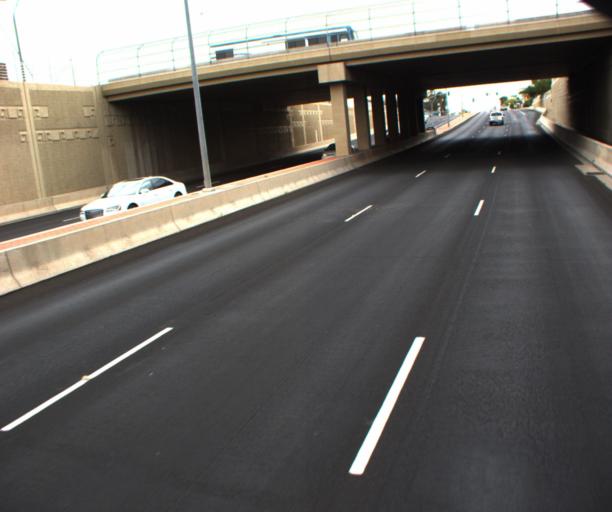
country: US
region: Arizona
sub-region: Maricopa County
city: Mesa
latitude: 33.4083
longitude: -111.8401
